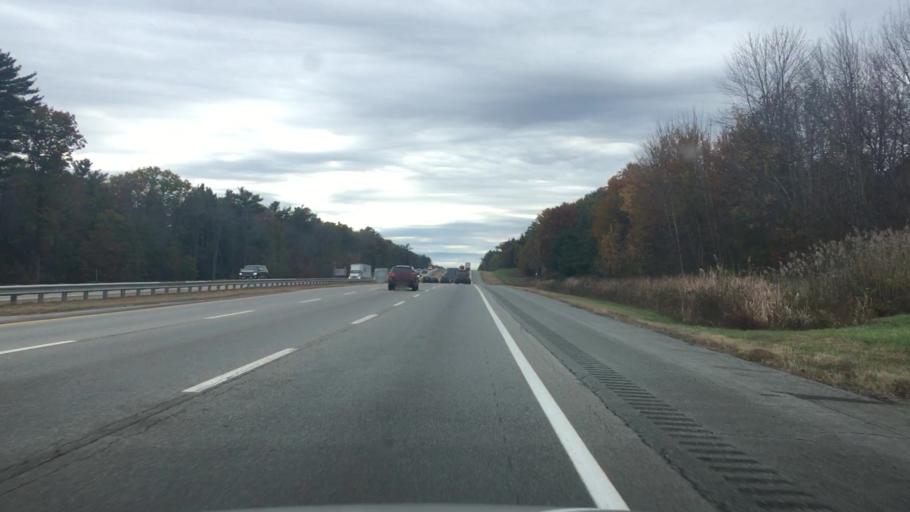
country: US
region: Maine
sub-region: Cumberland County
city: West Scarborough
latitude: 43.5743
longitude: -70.4036
